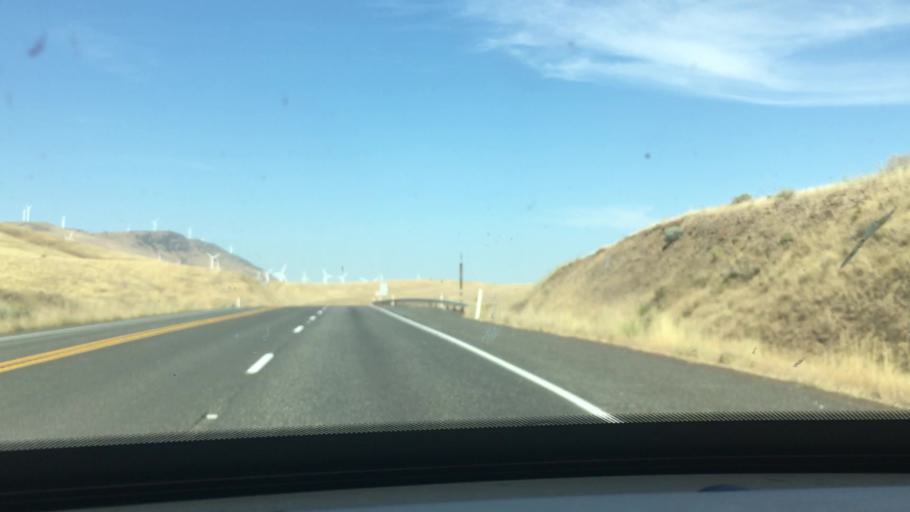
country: US
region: Washington
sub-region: Klickitat County
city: Goldendale
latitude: 45.7052
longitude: -120.8148
